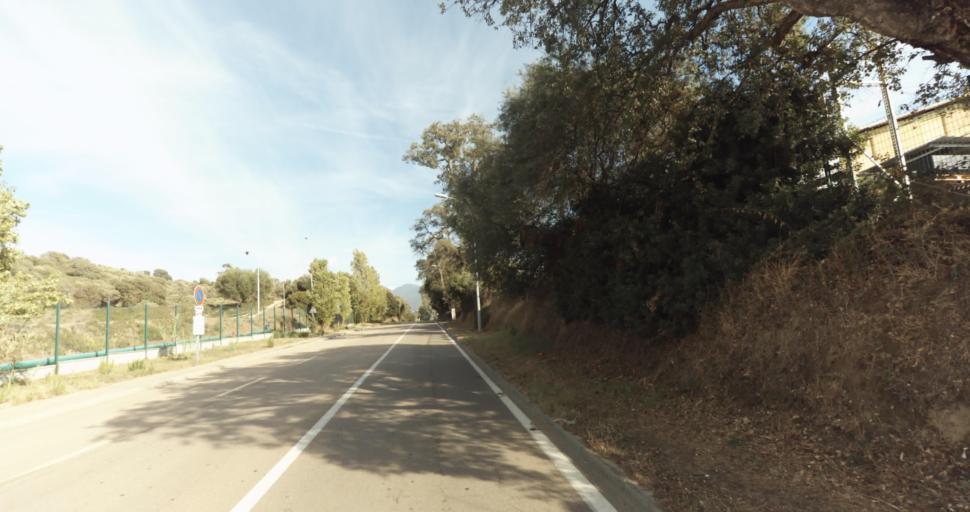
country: FR
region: Corsica
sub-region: Departement de la Corse-du-Sud
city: Afa
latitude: 41.9290
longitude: 8.7918
